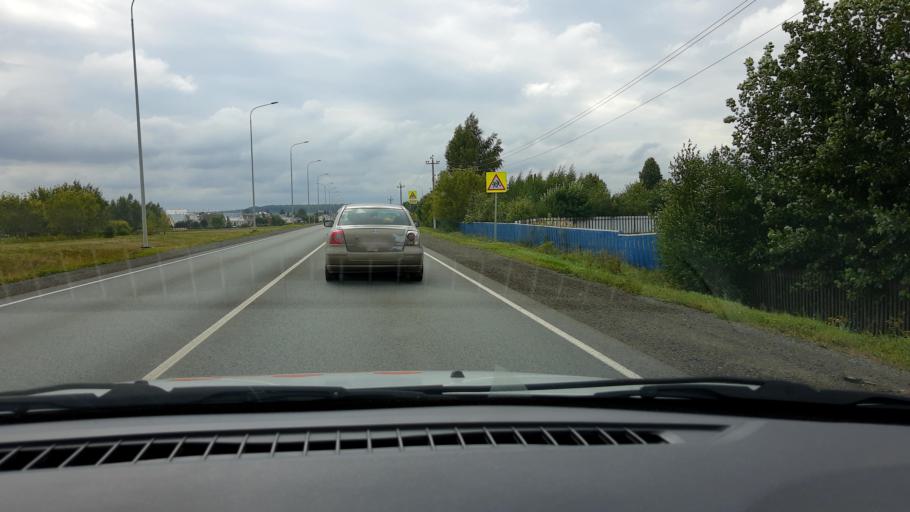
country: RU
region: Tatarstan
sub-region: Alekseyevskiy Rayon
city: Alekseyevskoye
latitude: 55.3028
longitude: 50.1310
